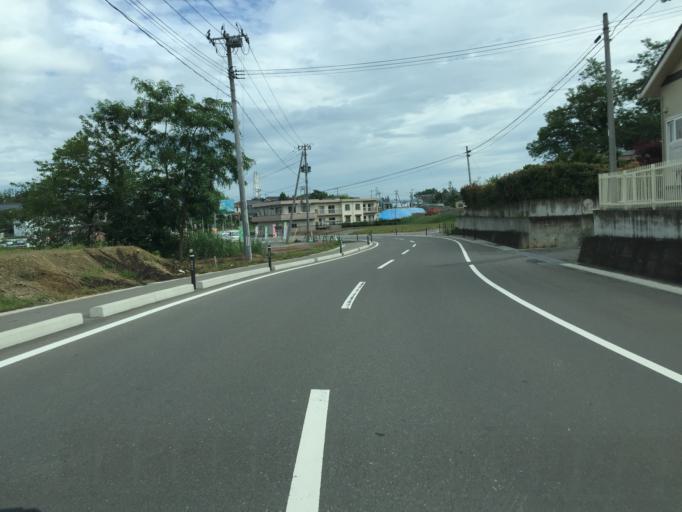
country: JP
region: Miyagi
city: Marumori
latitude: 37.8195
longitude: 140.9473
